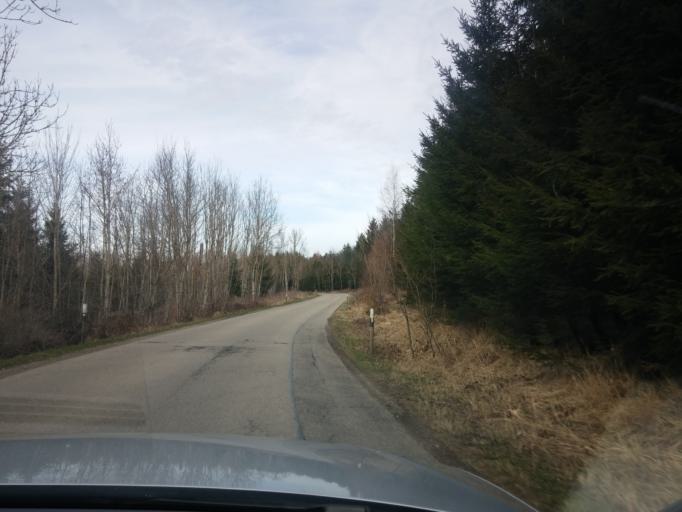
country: DE
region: Bavaria
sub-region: Swabia
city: Woringen
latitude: 47.9149
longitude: 10.1839
